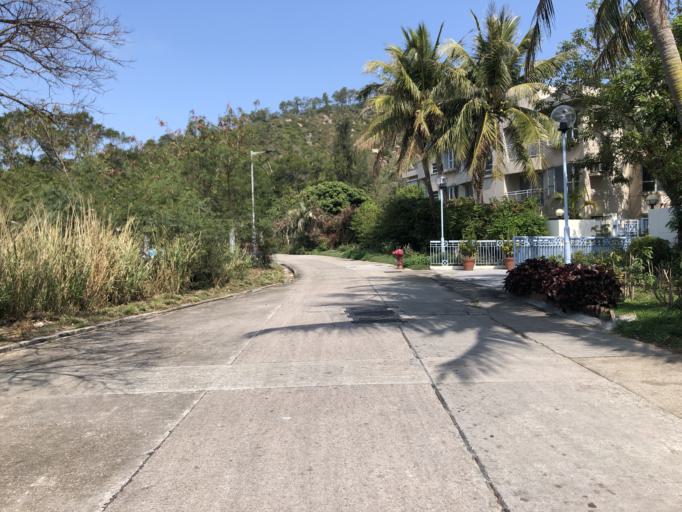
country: HK
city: Yung Shue Wan
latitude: 22.2172
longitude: 114.0268
